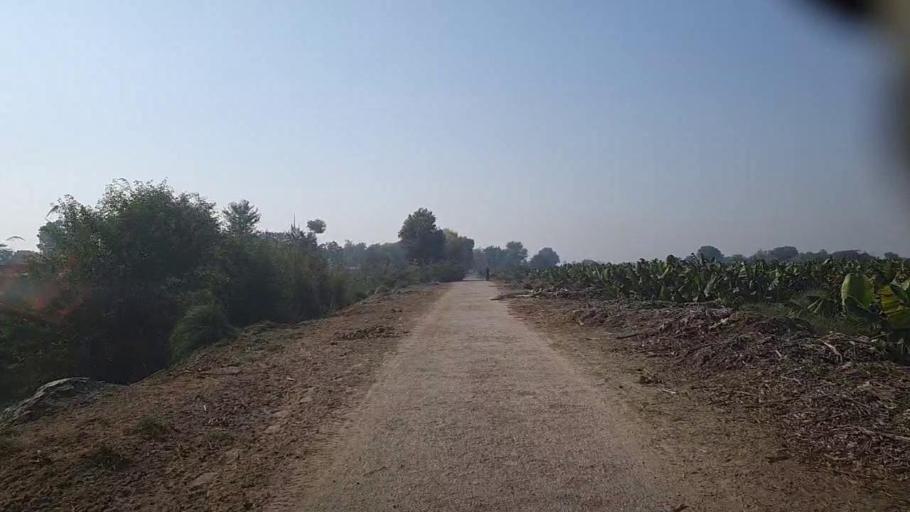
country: PK
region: Sindh
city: Kandiari
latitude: 27.0084
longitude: 68.4972
